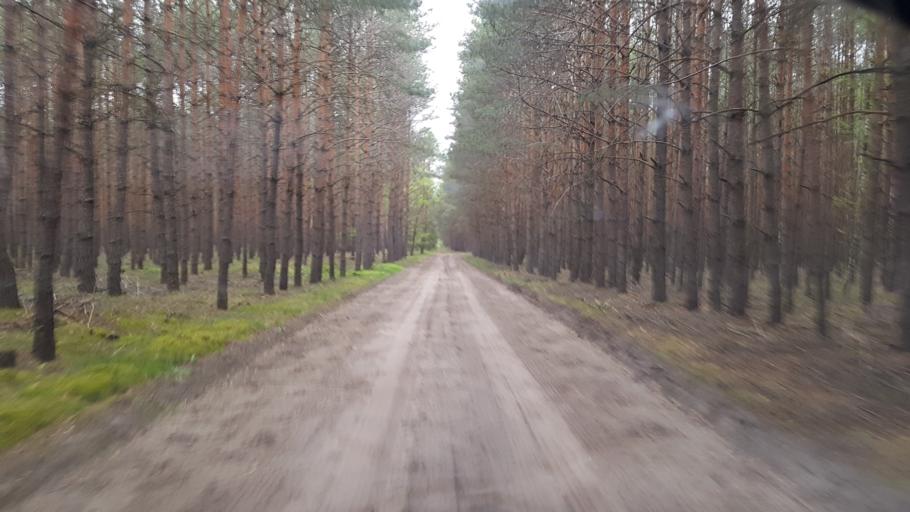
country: DE
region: Brandenburg
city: Schonewalde
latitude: 51.7044
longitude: 13.5238
